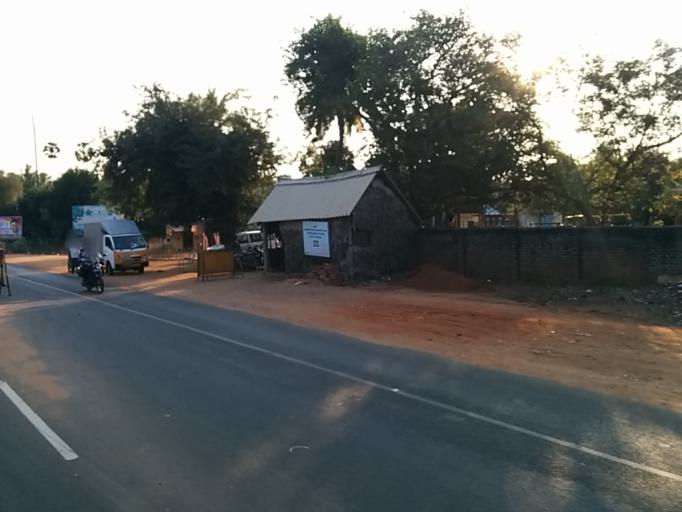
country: IN
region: Tamil Nadu
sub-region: Villupuram
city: Auroville
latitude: 11.9828
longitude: 79.8451
